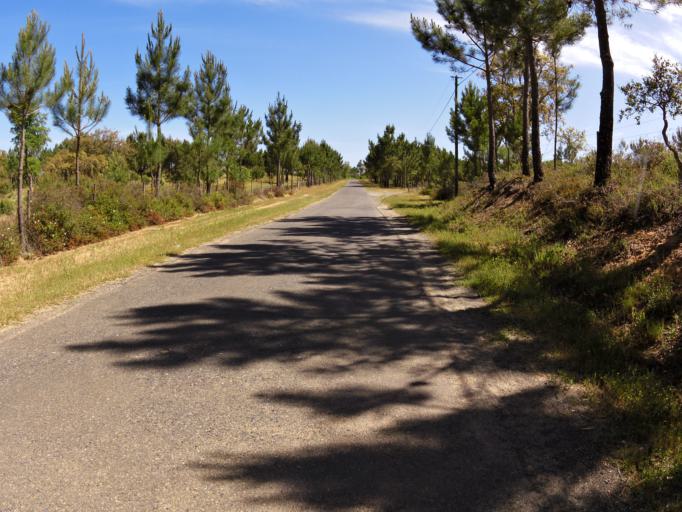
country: PT
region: Setubal
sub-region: Santiago do Cacem
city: Santiago do Cacem
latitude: 37.9412
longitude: -8.7354
